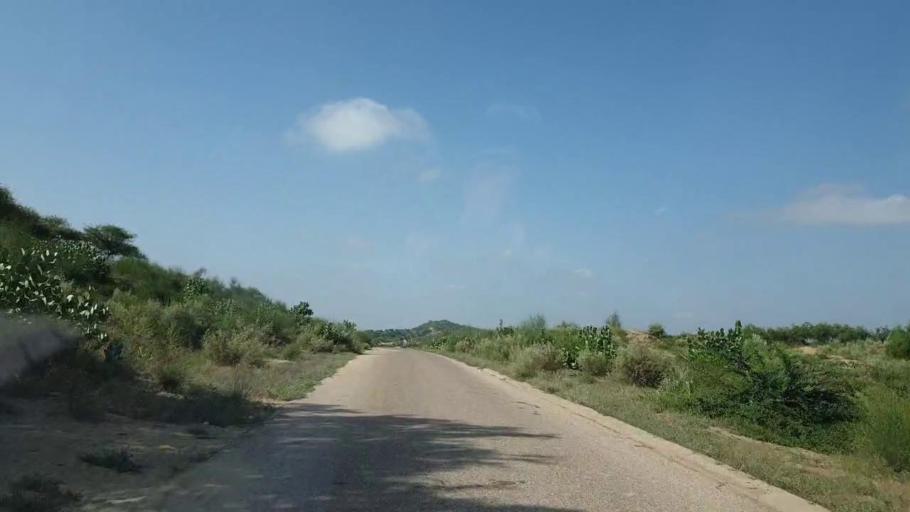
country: PK
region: Sindh
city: Mithi
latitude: 24.5555
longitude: 69.8938
